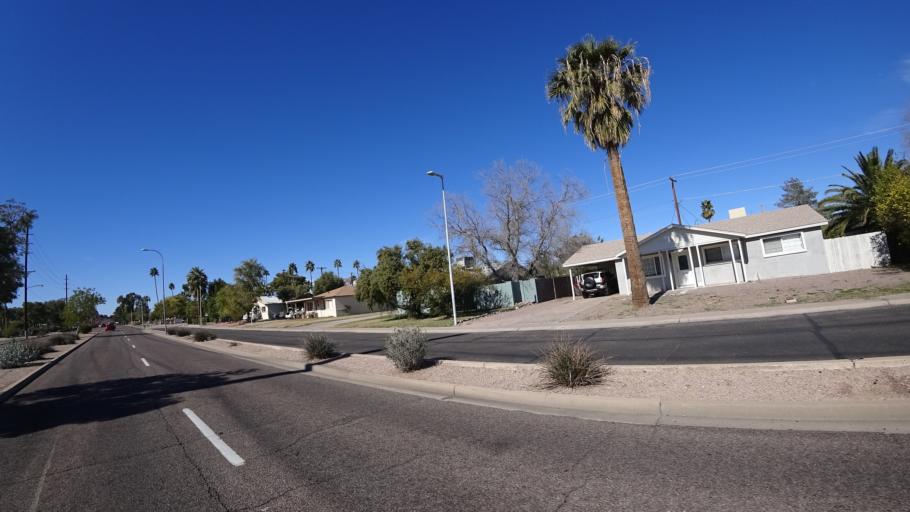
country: US
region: Arizona
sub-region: Maricopa County
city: Tempe
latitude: 33.4513
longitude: -111.9233
